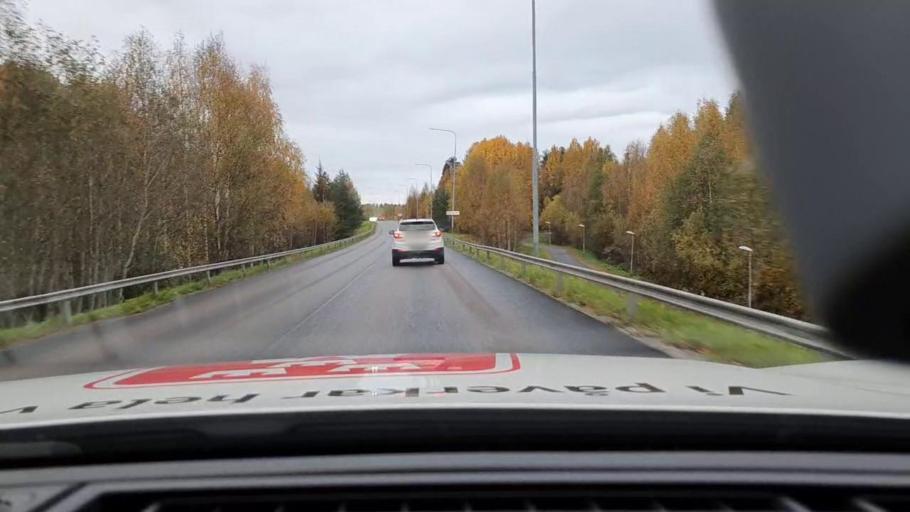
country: SE
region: Norrbotten
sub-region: Bodens Kommun
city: Saevast
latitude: 65.7659
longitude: 21.7391
